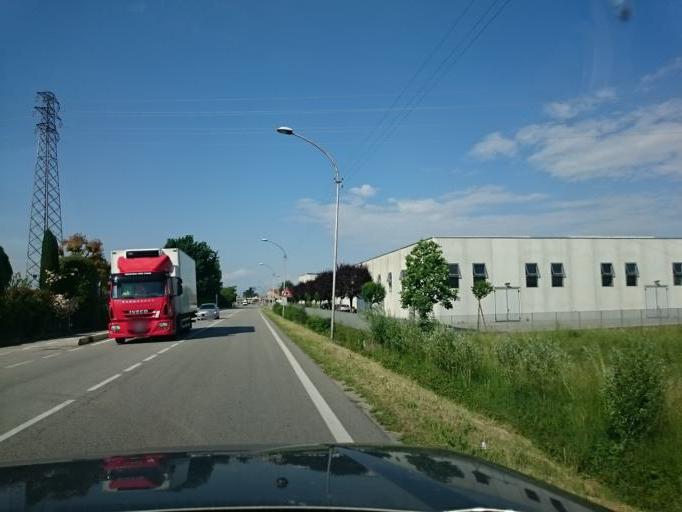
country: IT
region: Veneto
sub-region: Provincia di Vicenza
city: Montegalda
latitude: 45.4569
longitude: 11.6891
